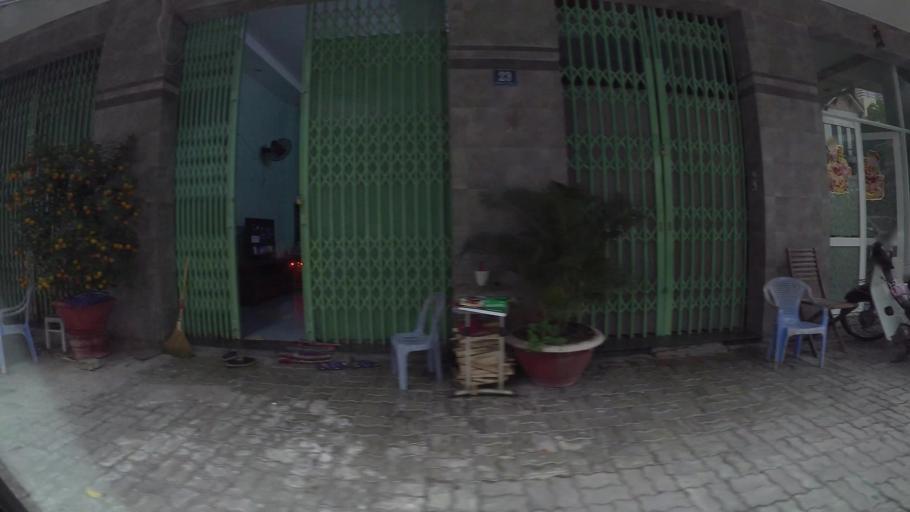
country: VN
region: Da Nang
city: Cam Le
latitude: 16.0436
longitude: 108.2090
